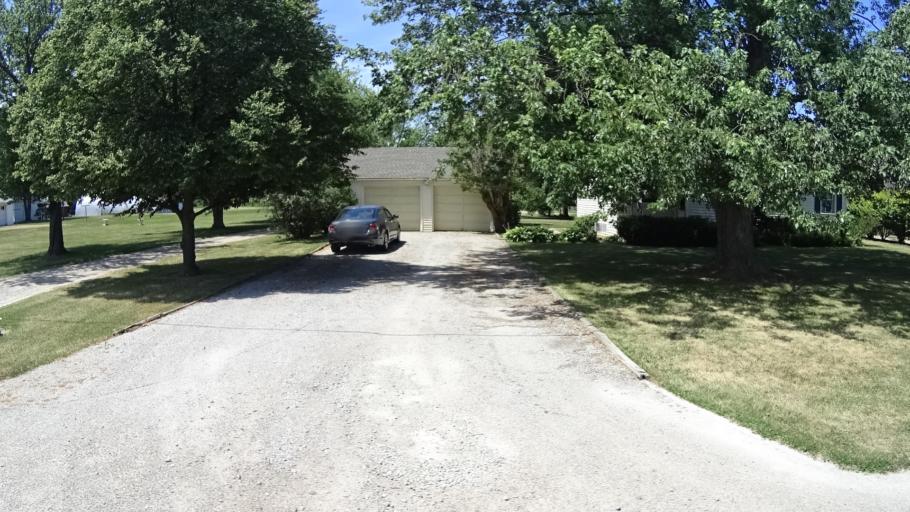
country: US
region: Ohio
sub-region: Erie County
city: Sandusky
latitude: 41.3952
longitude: -82.6960
